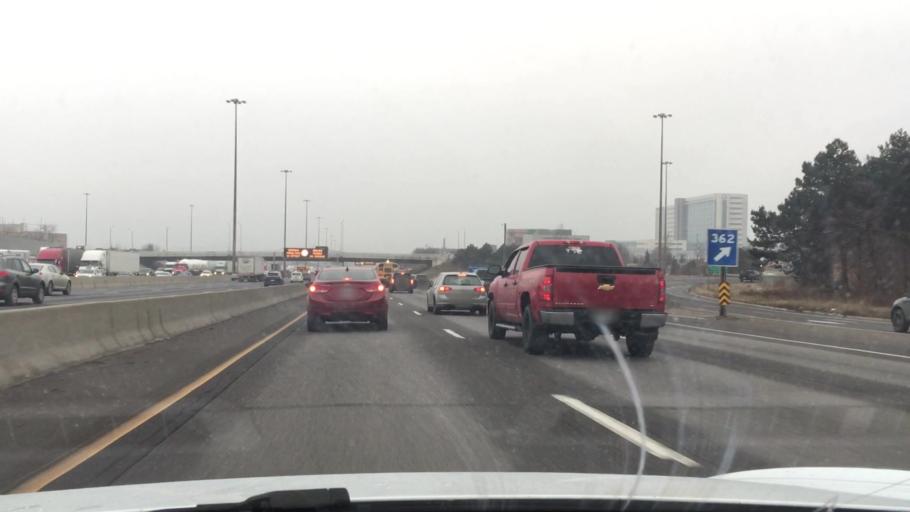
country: CA
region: Ontario
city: Toronto
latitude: 43.7240
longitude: -79.4776
